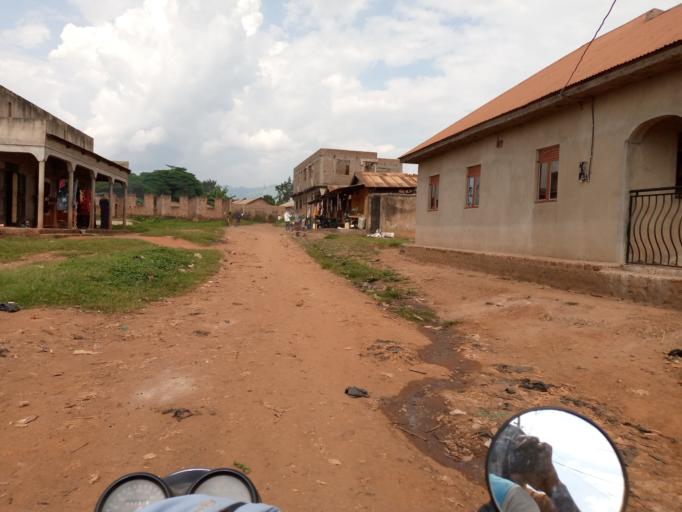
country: UG
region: Eastern Region
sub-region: Mbale District
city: Mbale
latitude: 1.0812
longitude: 34.1640
